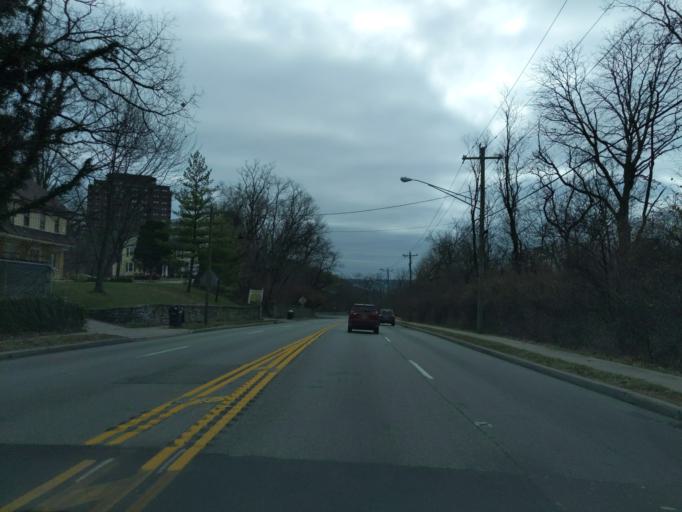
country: US
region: Ohio
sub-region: Hamilton County
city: Finneytown
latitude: 39.1871
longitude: -84.5451
